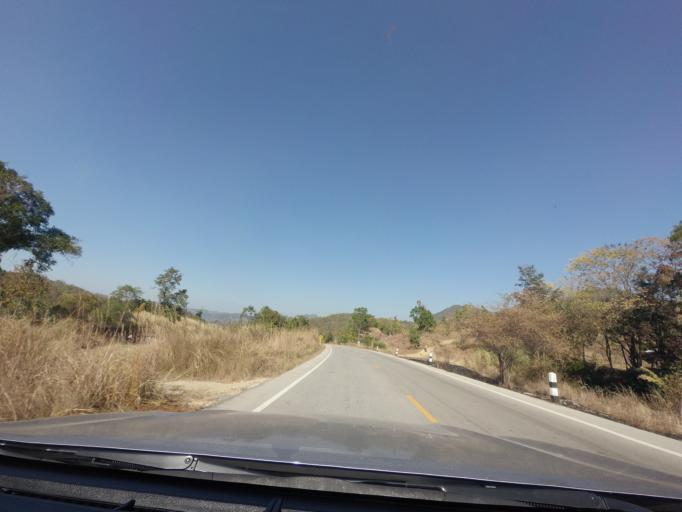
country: TH
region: Lampang
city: Chae Hom
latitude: 18.5729
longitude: 99.6265
